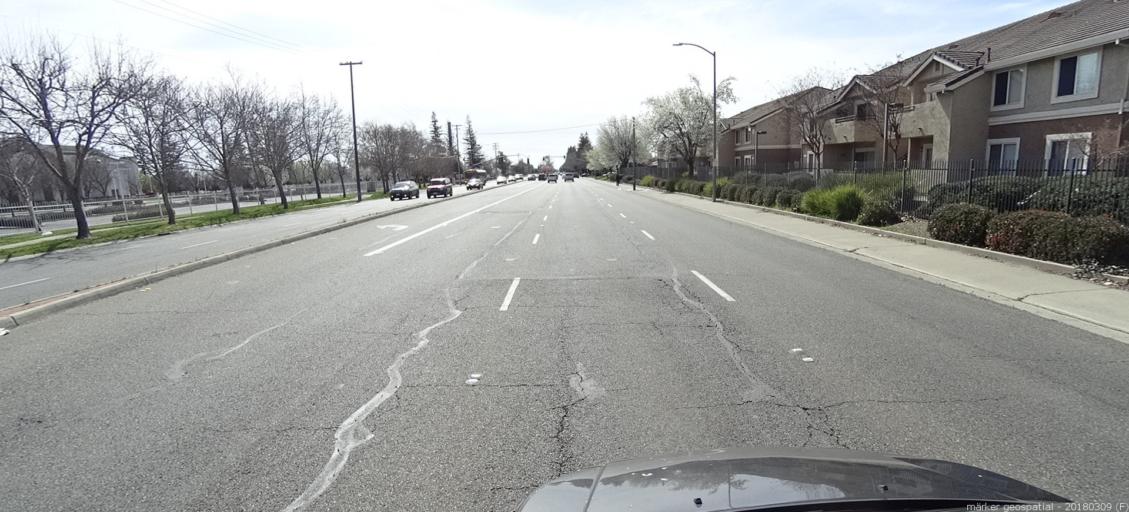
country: US
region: California
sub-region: Sacramento County
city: Vineyard
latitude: 38.4671
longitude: -121.3719
